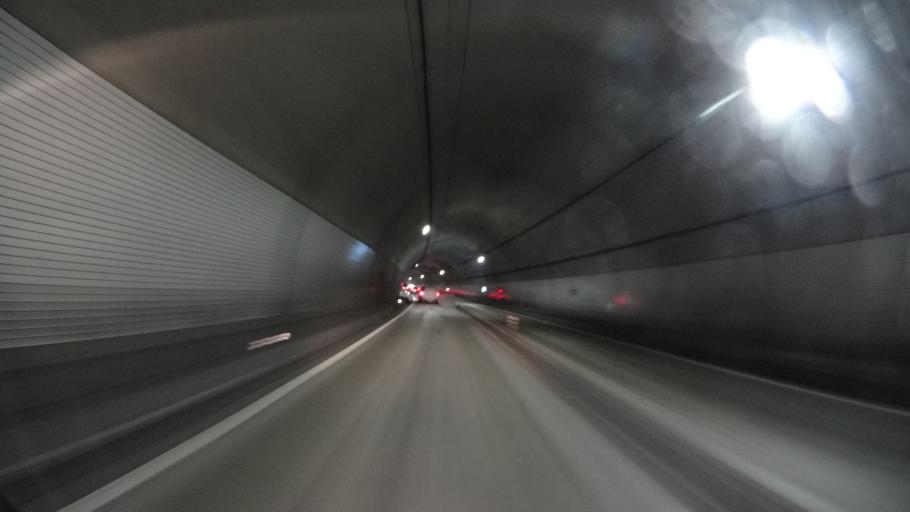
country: JP
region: Gunma
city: Numata
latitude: 36.6616
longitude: 139.1687
